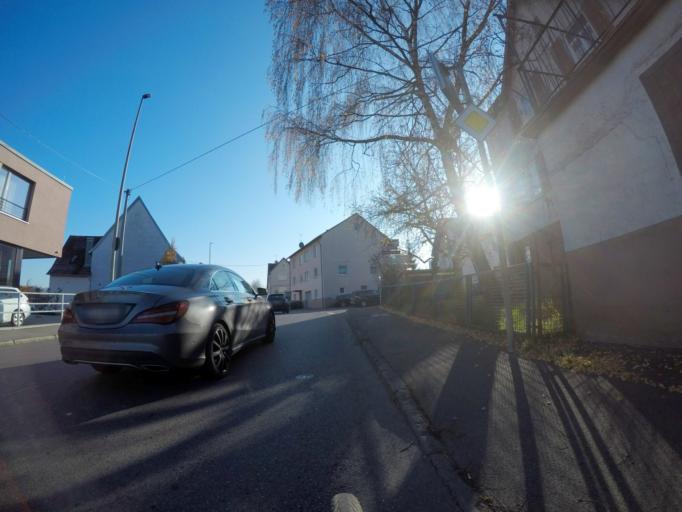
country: DE
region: Baden-Wuerttemberg
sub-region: Tuebingen Region
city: Reutlingen
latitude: 48.5208
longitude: 9.2273
